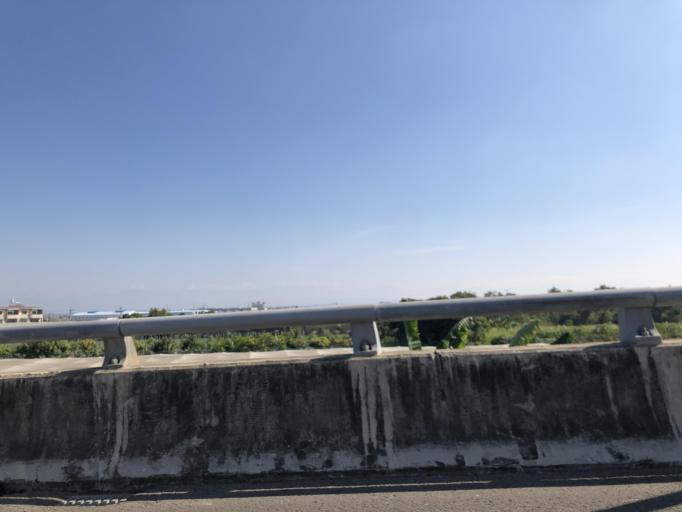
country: TW
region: Taiwan
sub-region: Tainan
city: Tainan
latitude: 23.0183
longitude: 120.2890
